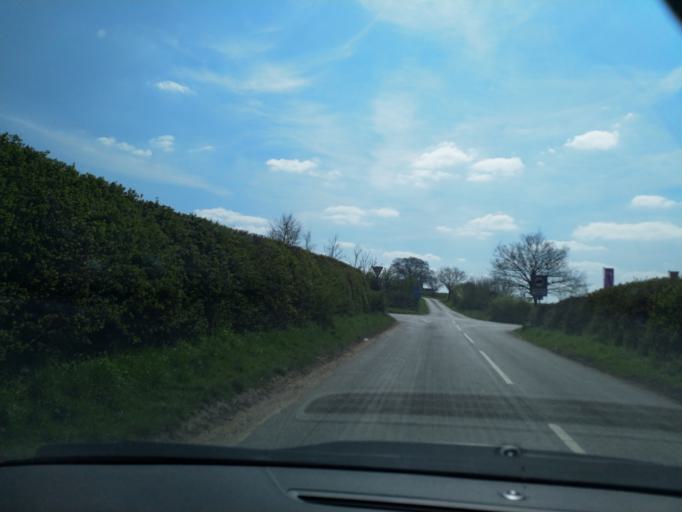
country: GB
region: England
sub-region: Warwickshire
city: Stratford-upon-Avon
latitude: 52.1905
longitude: -1.6723
